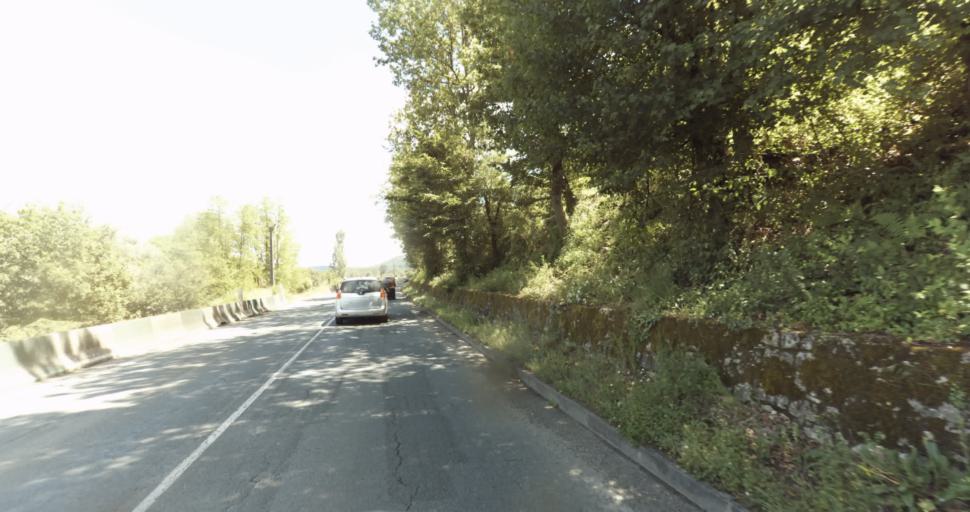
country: FR
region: Aquitaine
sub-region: Departement de la Dordogne
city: Le Bugue
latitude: 44.8405
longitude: 0.9321
